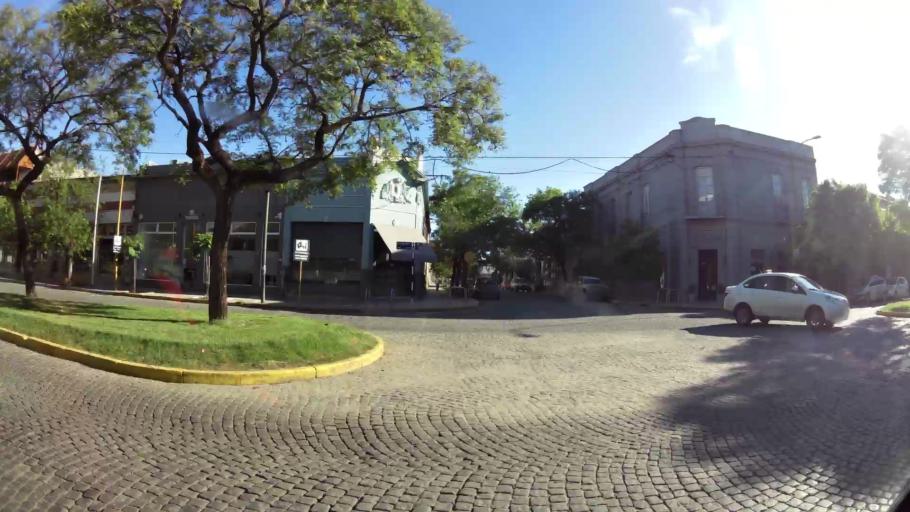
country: AR
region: Cordoba
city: San Francisco
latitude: -31.4303
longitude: -62.0885
